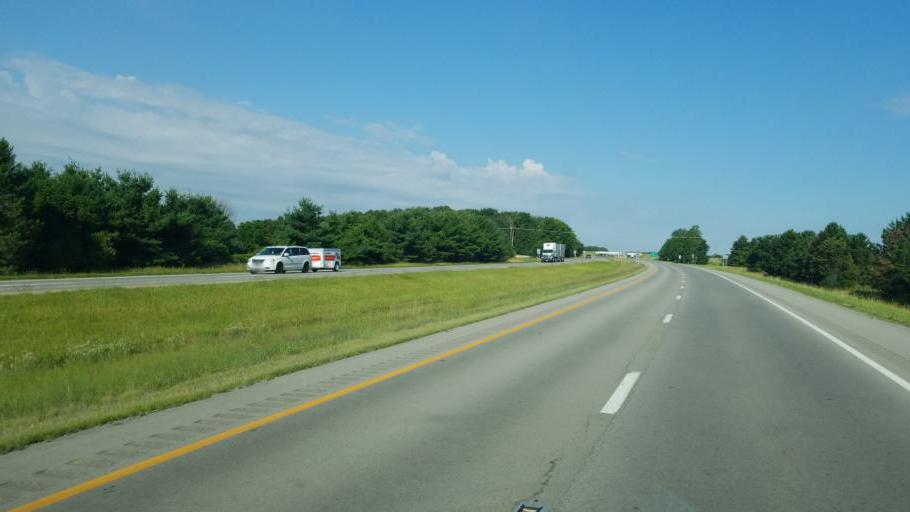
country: US
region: Ohio
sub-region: Hancock County
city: Findlay
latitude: 40.9855
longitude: -83.5618
